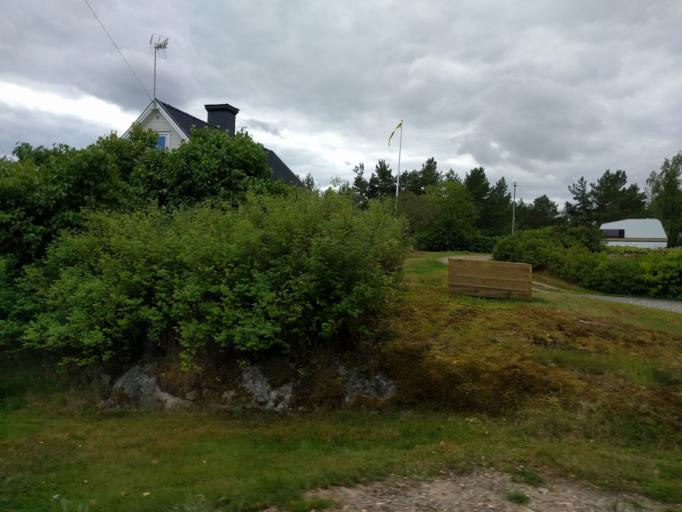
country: SE
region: Soedermanland
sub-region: Nykopings Kommun
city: Svalsta
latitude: 58.5026
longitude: 16.8579
